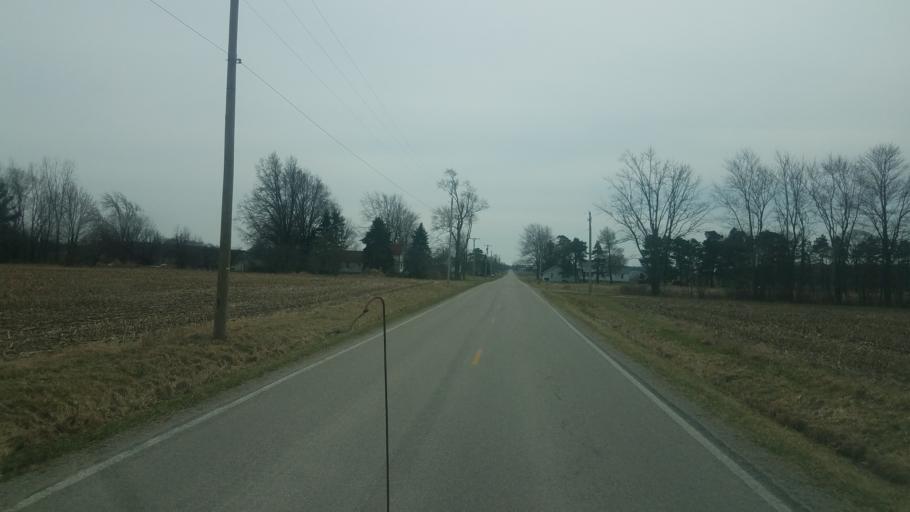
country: US
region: Ohio
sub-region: Huron County
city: Wakeman
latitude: 41.1985
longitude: -82.4907
